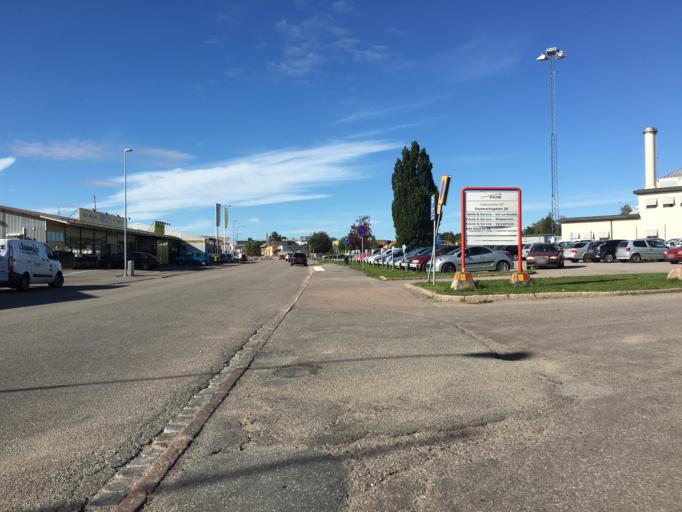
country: SE
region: Uppsala
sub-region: Uppsala Kommun
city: Uppsala
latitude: 59.8499
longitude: 17.6733
